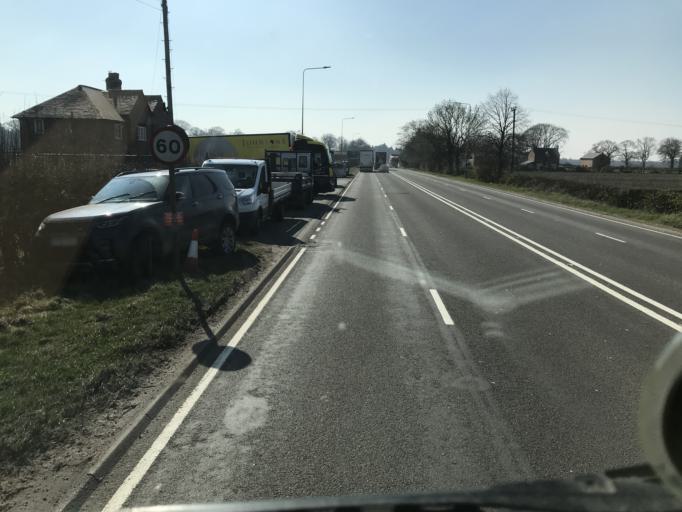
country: GB
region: England
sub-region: Cheshire East
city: Mere
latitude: 53.3053
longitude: -2.4185
